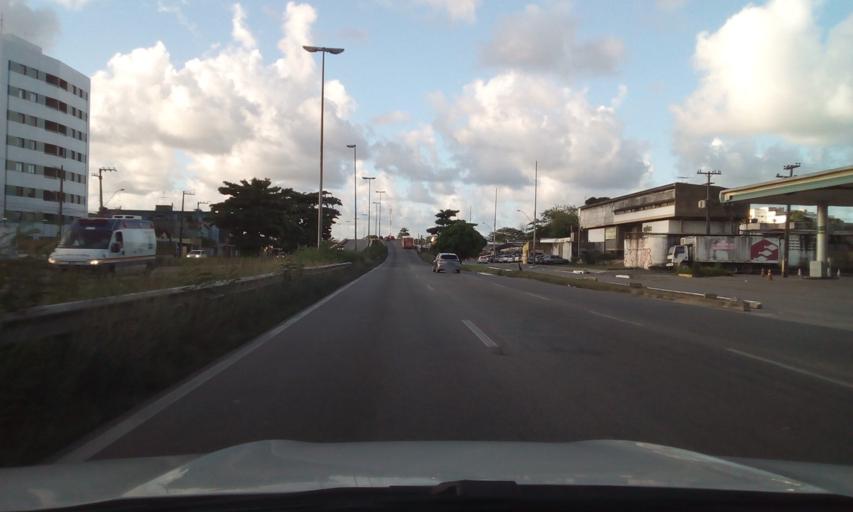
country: BR
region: Pernambuco
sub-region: Recife
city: Recife
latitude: -8.0417
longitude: -34.9429
